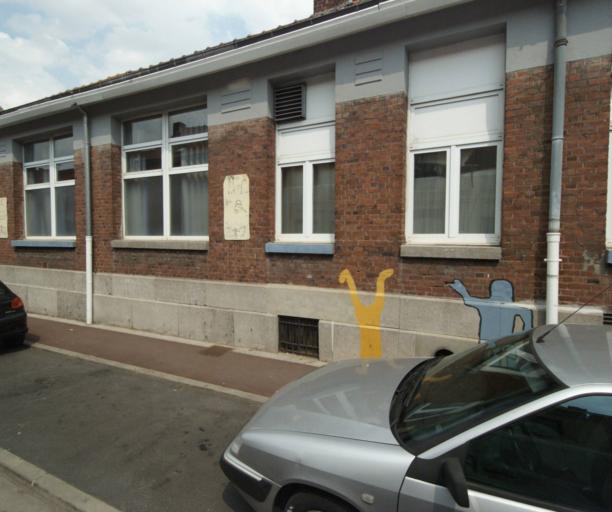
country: FR
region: Nord-Pas-de-Calais
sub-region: Departement du Nord
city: Tourcoing
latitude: 50.7321
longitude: 3.1521
